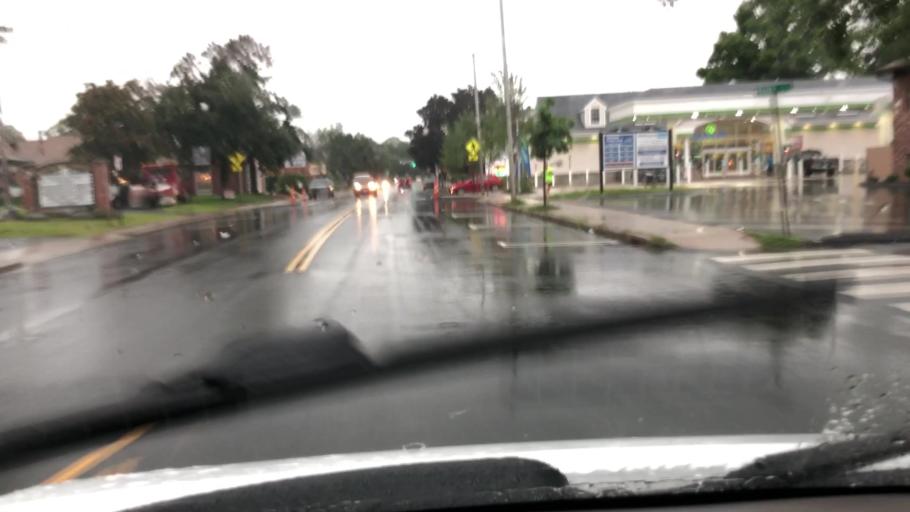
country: US
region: Massachusetts
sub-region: Hampshire County
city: Northampton
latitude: 42.3349
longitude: -72.6684
